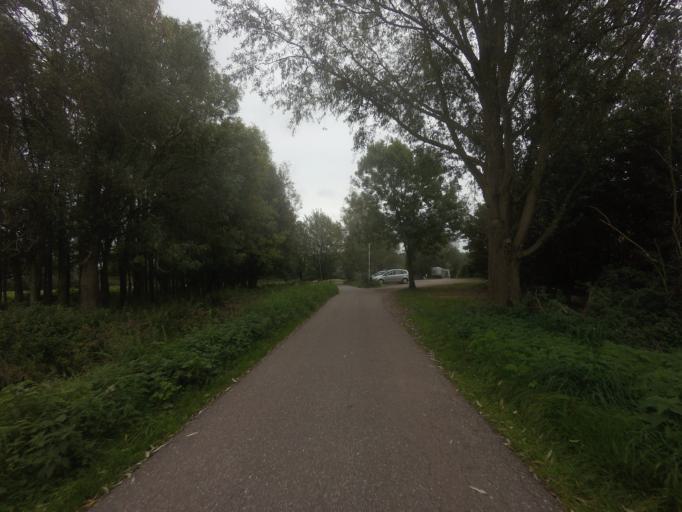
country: NL
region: Friesland
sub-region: Gemeente Leeuwarden
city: Bilgaard
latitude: 53.2199
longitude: 5.7921
